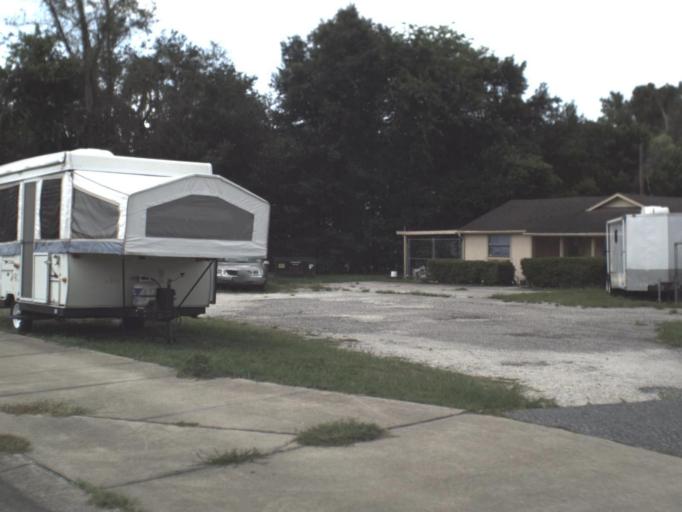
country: US
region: Florida
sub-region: Citrus County
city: Inverness Highlands South
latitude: 28.7967
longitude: -82.3063
